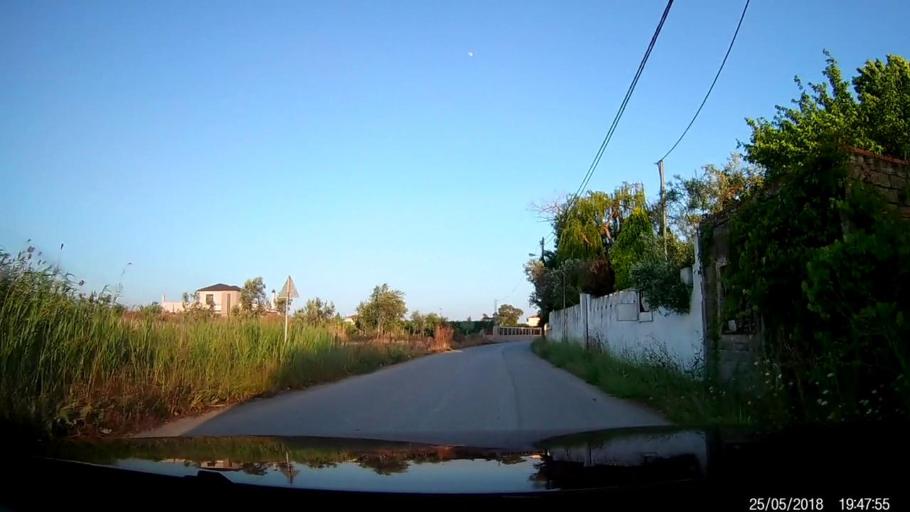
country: GR
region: Central Greece
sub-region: Nomos Evvoias
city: Ayios Nikolaos
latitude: 38.4200
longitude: 23.6368
